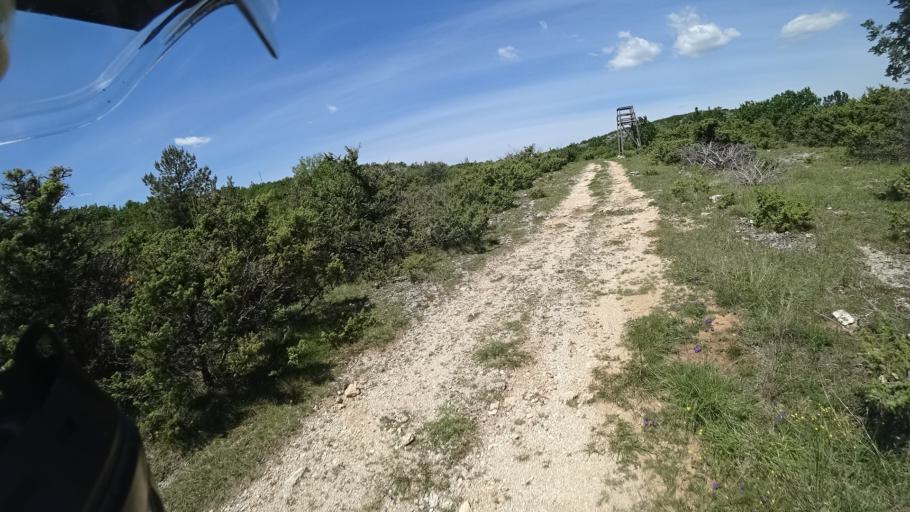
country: HR
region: Sibensko-Kniniska
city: Knin
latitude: 44.0322
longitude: 16.2533
